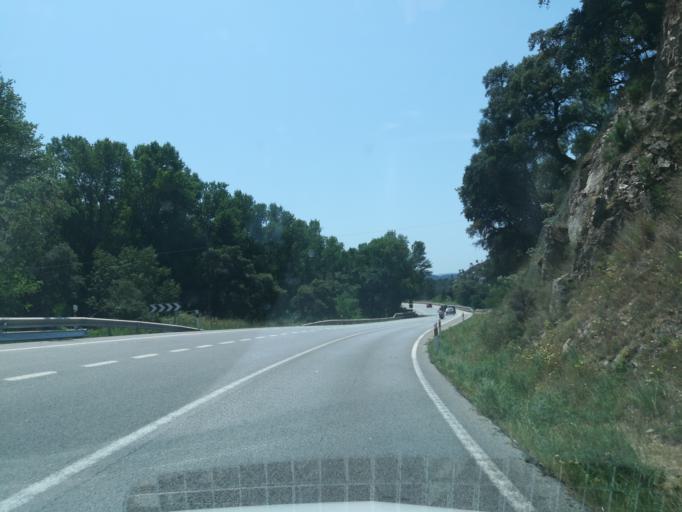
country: ES
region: Catalonia
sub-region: Provincia de Girona
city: la Jonquera
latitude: 42.4509
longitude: 2.8665
